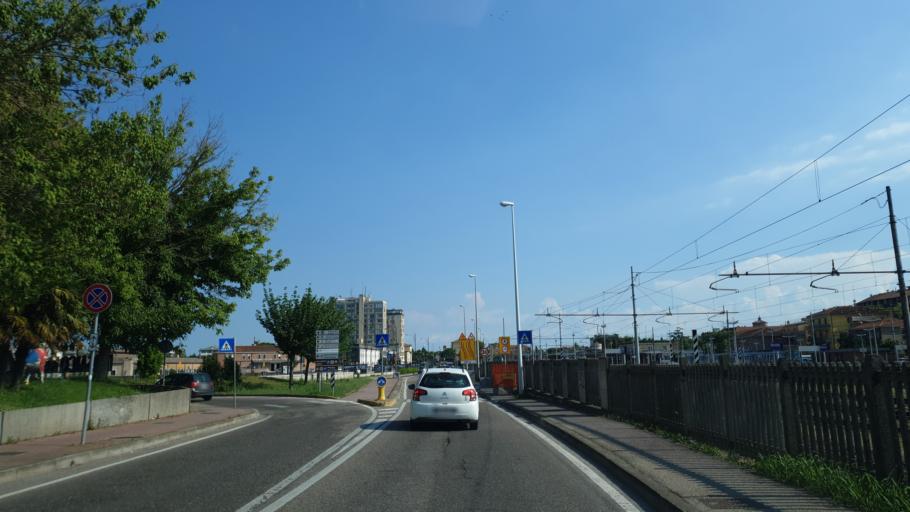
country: IT
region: Emilia-Romagna
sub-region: Provincia di Ravenna
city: Ravenna
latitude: 44.4219
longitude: 12.2081
